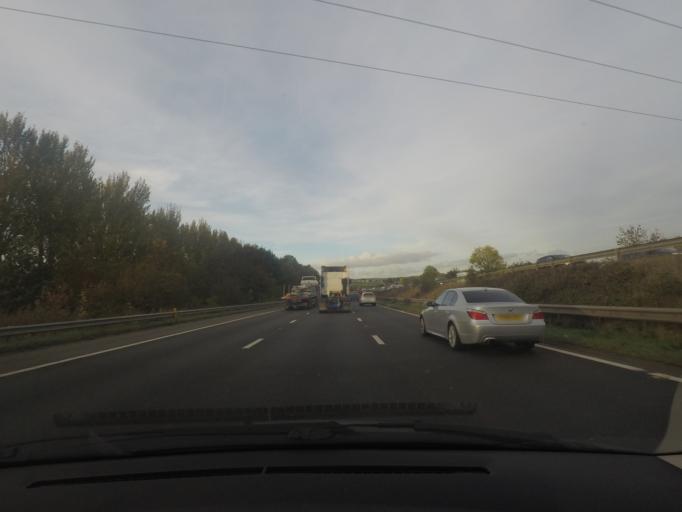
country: GB
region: England
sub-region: Barnsley
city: Darton
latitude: 53.5727
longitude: -1.5414
